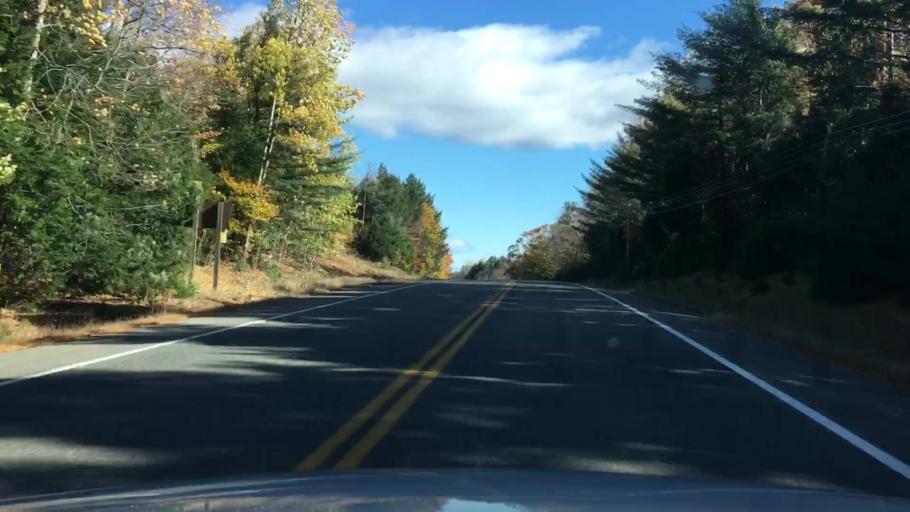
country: US
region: Maine
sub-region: Penobscot County
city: Millinocket
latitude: 45.6574
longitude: -68.6517
